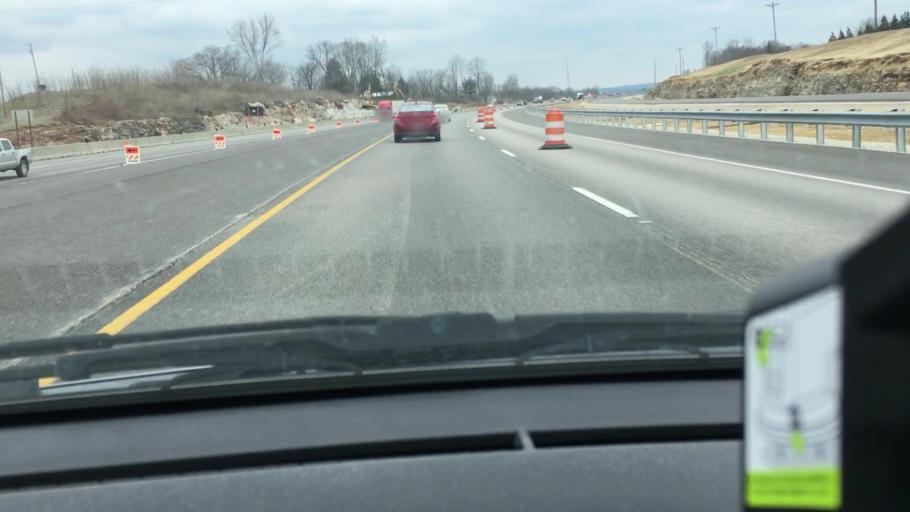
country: US
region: Indiana
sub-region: Monroe County
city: Bloomington
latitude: 39.2616
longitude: -86.5234
